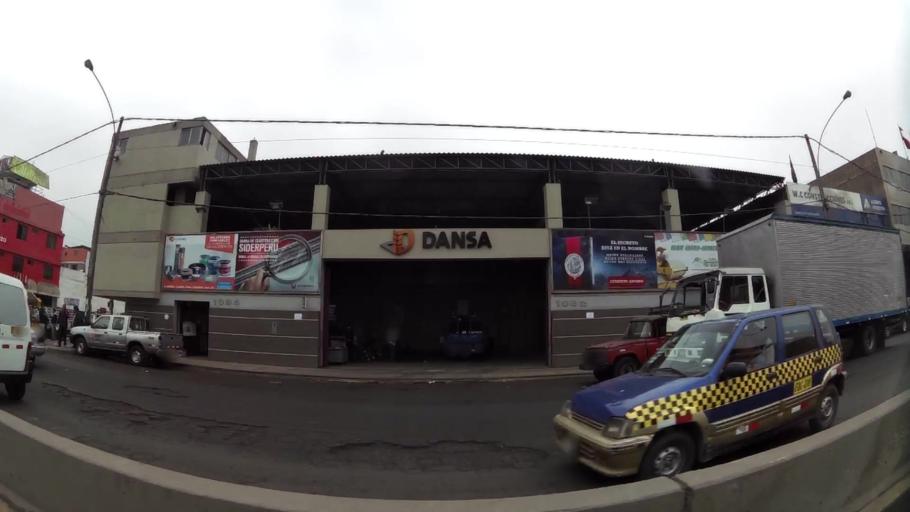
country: PE
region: Lima
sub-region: Lima
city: San Luis
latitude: -12.0695
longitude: -77.0170
